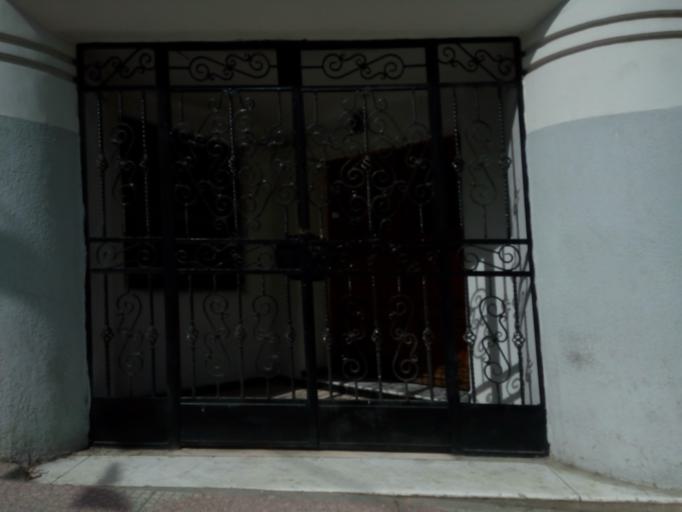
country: DZ
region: Constantine
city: Constantine
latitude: 36.3565
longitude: 6.6096
